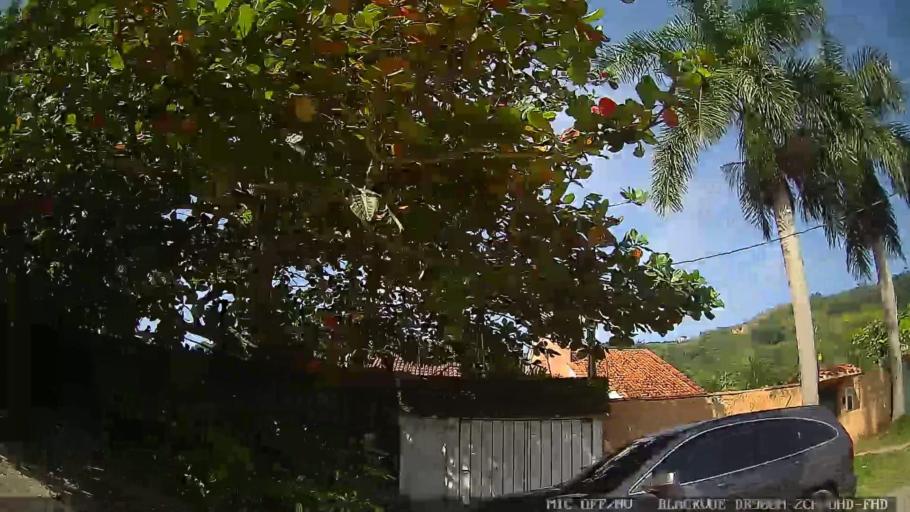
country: BR
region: Sao Paulo
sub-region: Guaruja
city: Guaruja
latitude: -23.9774
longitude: -46.1919
